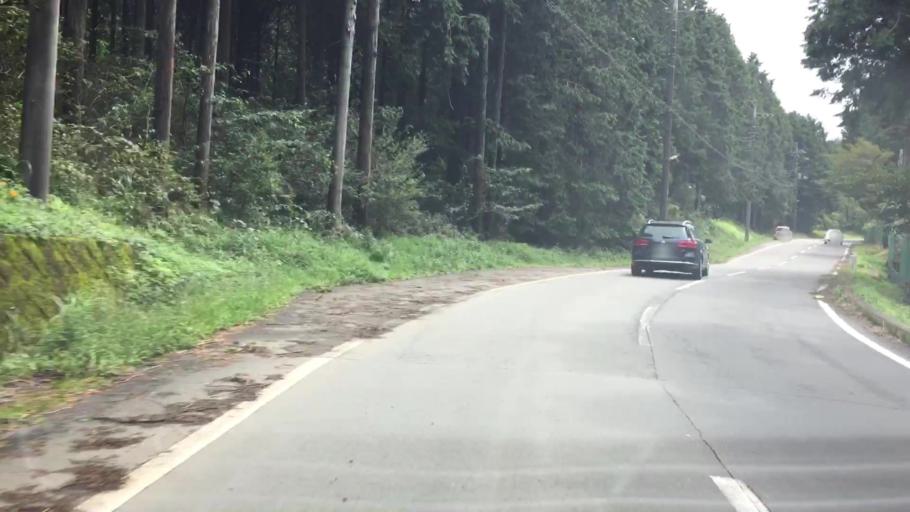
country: JP
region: Yamanashi
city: Fujikawaguchiko
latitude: 35.3933
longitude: 138.5697
